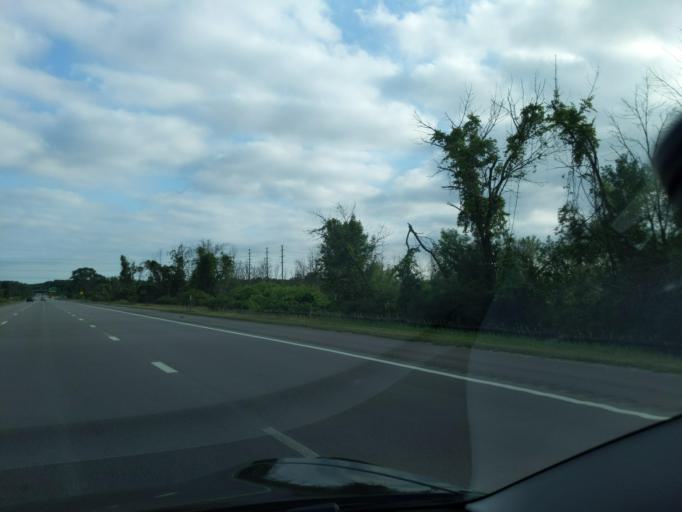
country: US
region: Michigan
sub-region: Muskegon County
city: Muskegon
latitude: 43.2669
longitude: -86.2049
